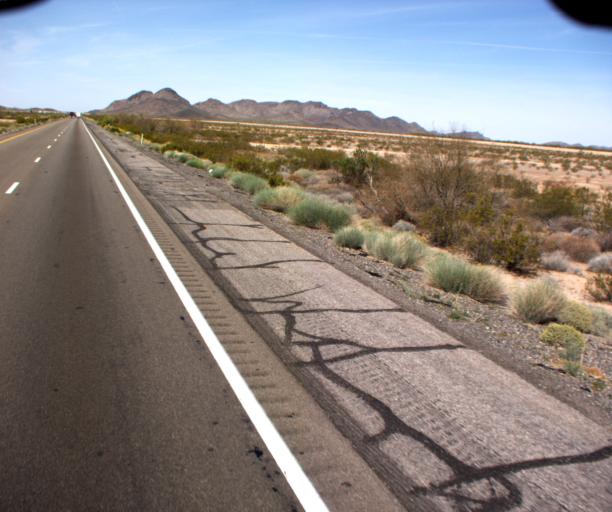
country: US
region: Arizona
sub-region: La Paz County
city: Salome
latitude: 33.6051
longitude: -113.5909
